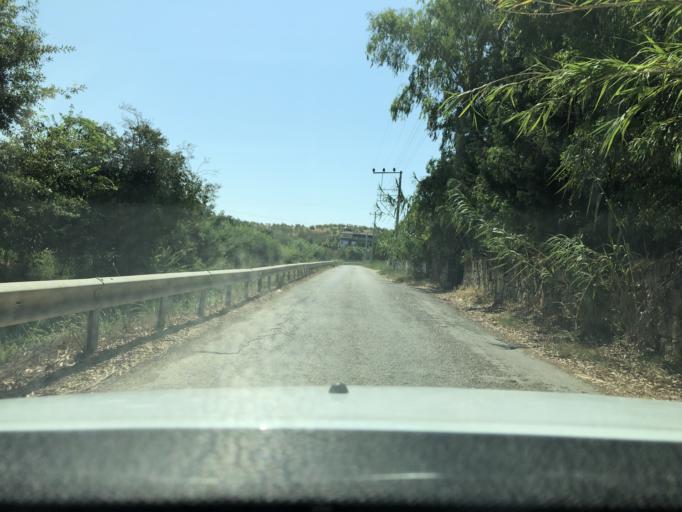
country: TR
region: Antalya
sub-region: Manavgat
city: Manavgat
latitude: 36.8039
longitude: 31.4680
